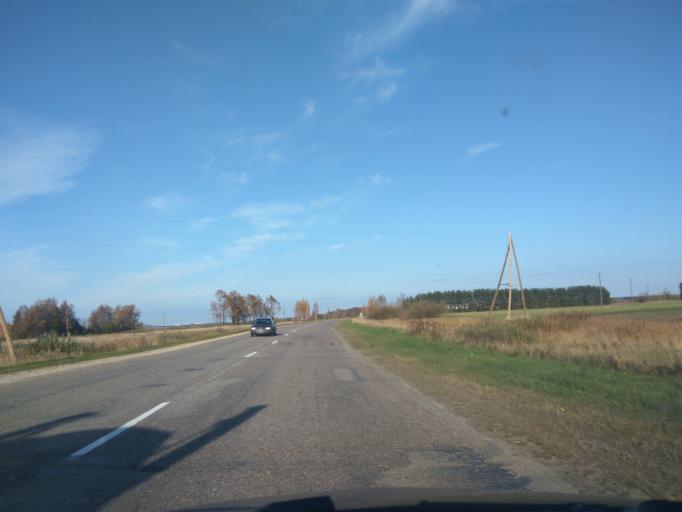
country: LV
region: Ventspils
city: Ventspils
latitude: 57.3336
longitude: 21.5639
